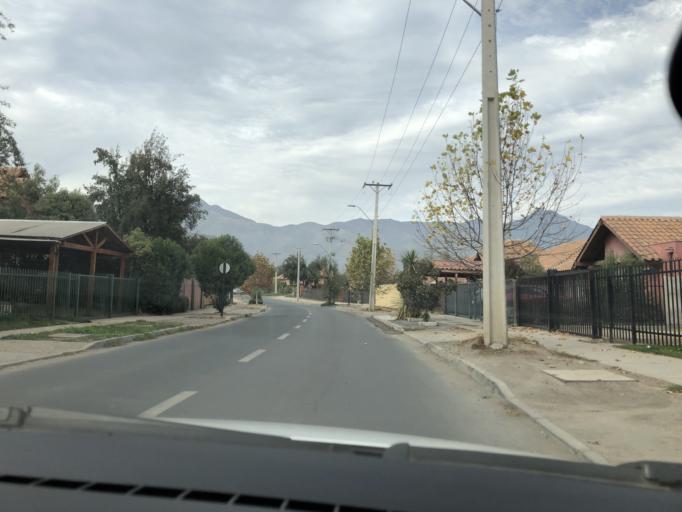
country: CL
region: Santiago Metropolitan
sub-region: Provincia de Cordillera
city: Puente Alto
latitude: -33.5862
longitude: -70.5131
